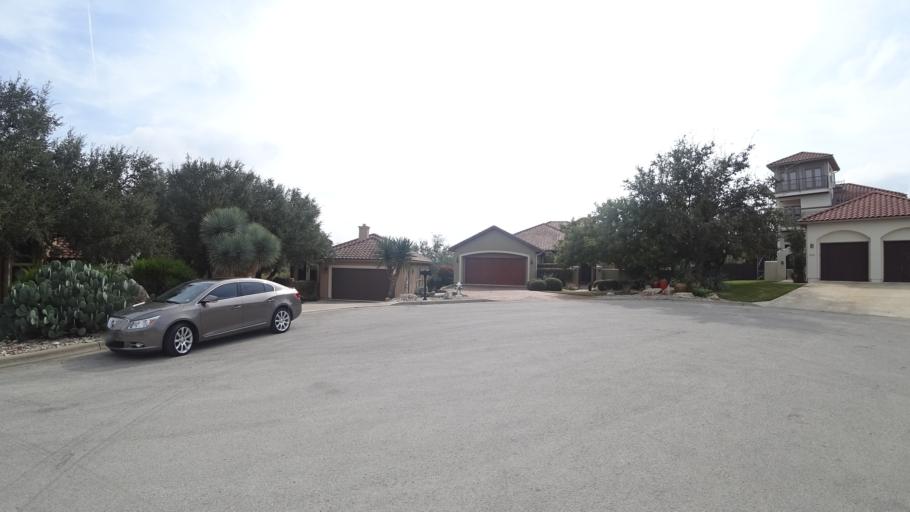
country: US
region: Texas
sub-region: Travis County
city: Hudson Bend
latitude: 30.3882
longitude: -97.9323
